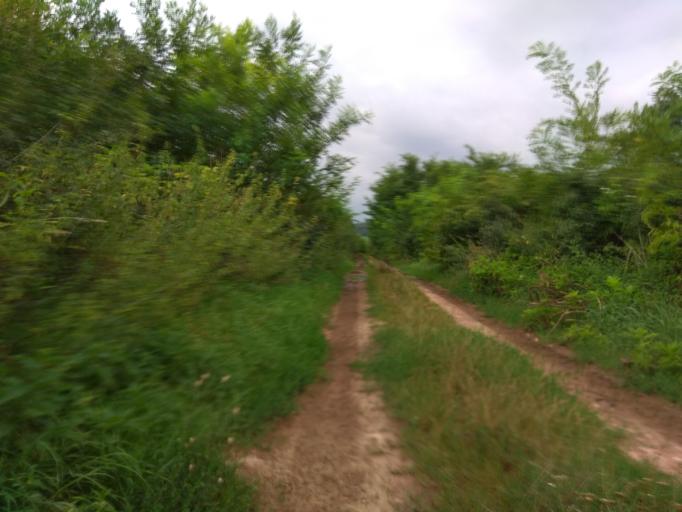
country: HU
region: Borsod-Abauj-Zemplen
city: Monok
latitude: 48.1777
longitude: 21.1231
